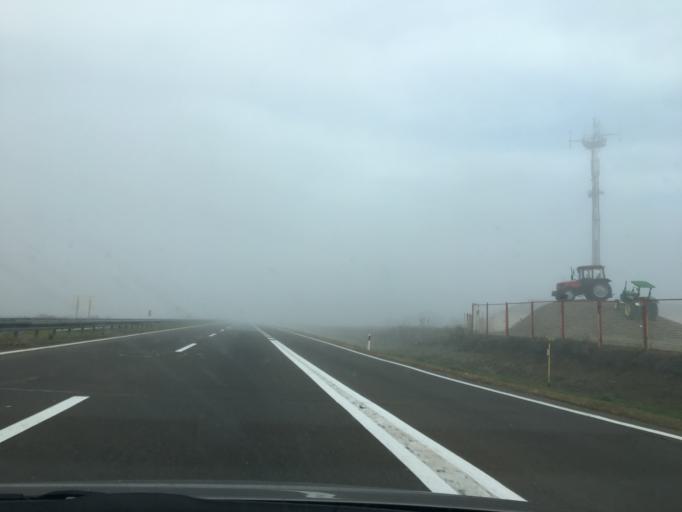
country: RS
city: Novi Banovci
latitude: 44.9445
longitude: 20.2799
